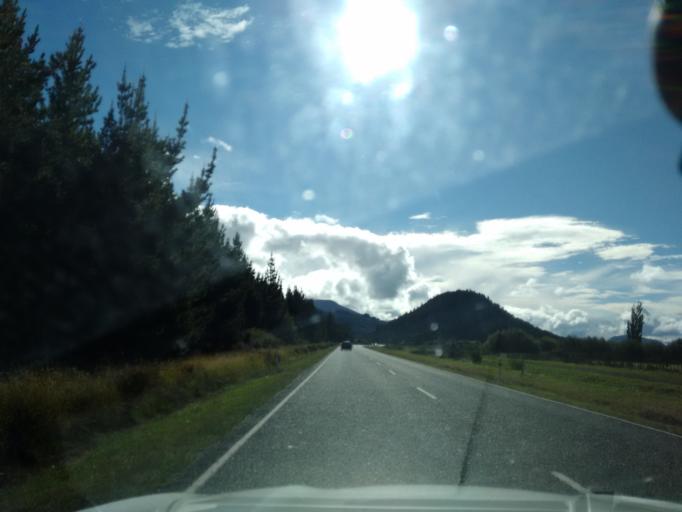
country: NZ
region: Waikato
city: Turangi
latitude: -38.9849
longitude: 175.7843
